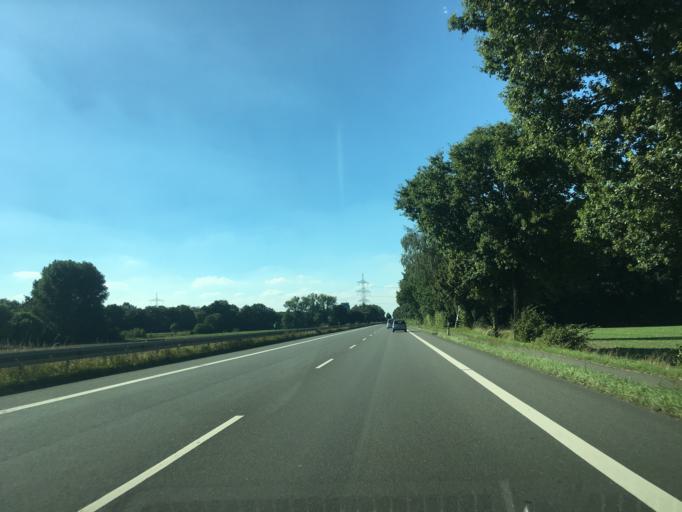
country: DE
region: North Rhine-Westphalia
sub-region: Regierungsbezirk Detmold
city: Harsewinkel
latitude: 51.8873
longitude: 8.2244
